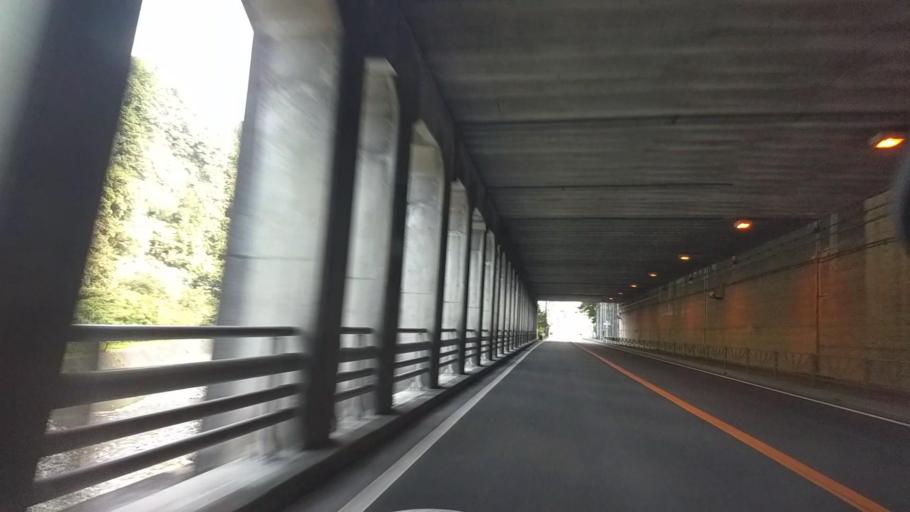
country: JP
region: Shizuoka
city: Fujinomiya
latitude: 35.3565
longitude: 138.4216
